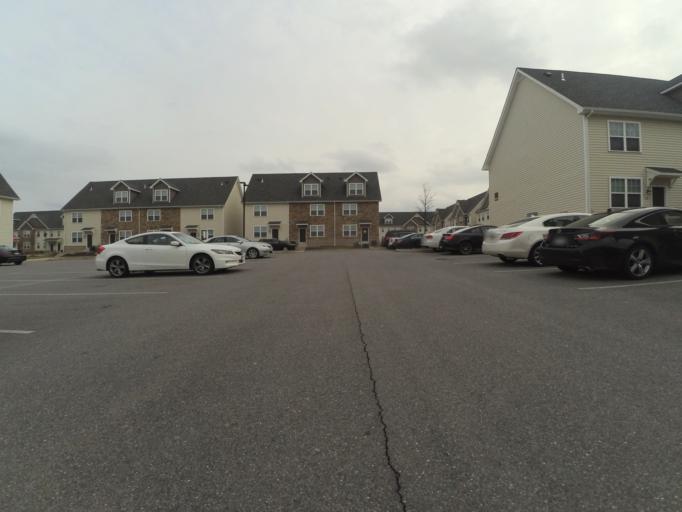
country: US
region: Pennsylvania
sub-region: Centre County
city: Park Forest Village
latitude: 40.7899
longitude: -77.8974
